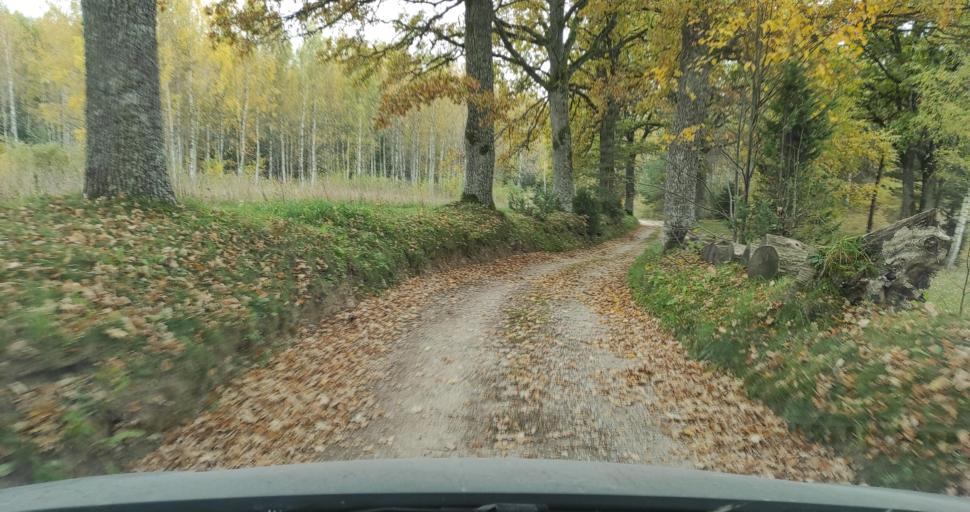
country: LV
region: Alsunga
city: Alsunga
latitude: 57.0359
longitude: 21.7045
